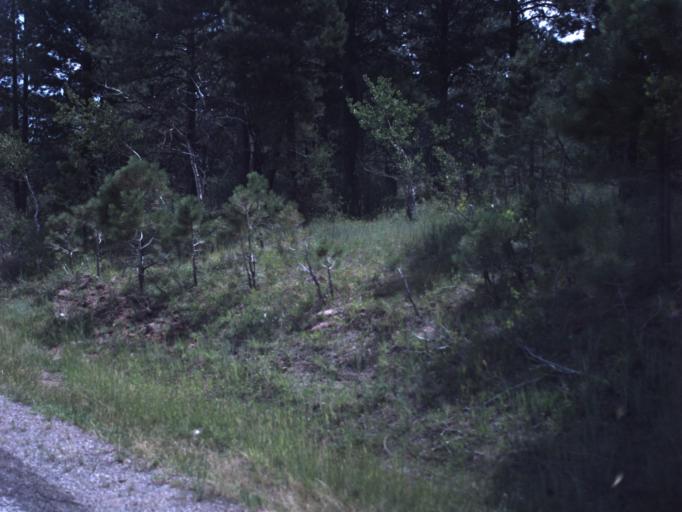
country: US
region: Utah
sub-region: Daggett County
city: Manila
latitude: 40.8662
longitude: -109.5179
